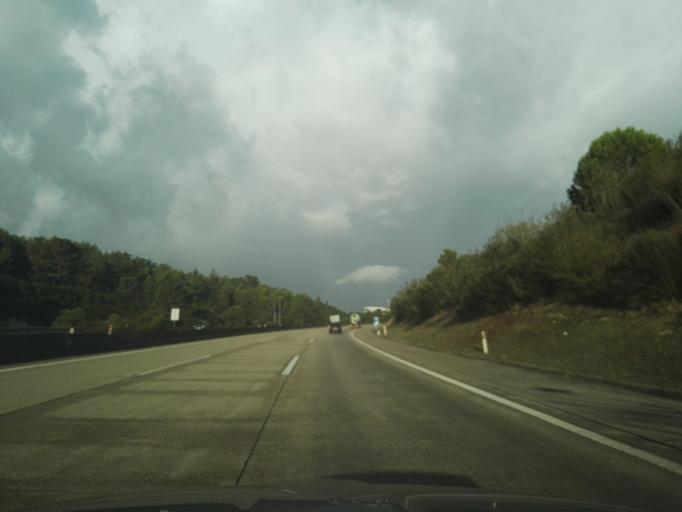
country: PT
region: Lisbon
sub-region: Vila Franca de Xira
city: Vialonga
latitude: 38.9064
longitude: -9.0619
